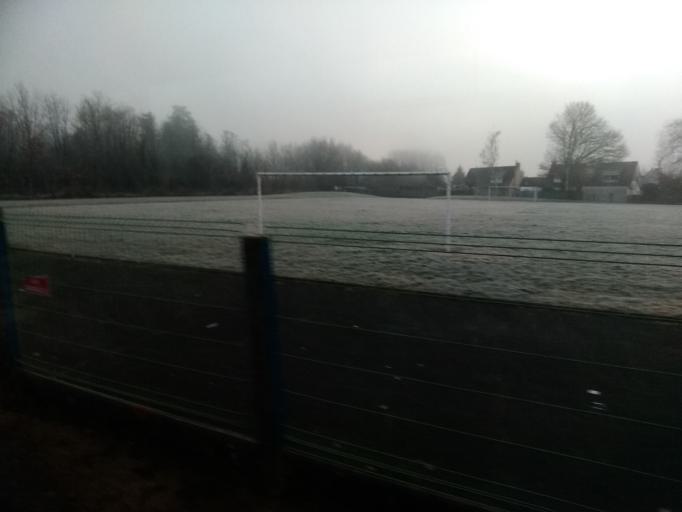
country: FR
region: Aquitaine
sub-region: Departement de la Dordogne
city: Terrasson-Lavilledieu
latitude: 45.1328
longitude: 1.2796
